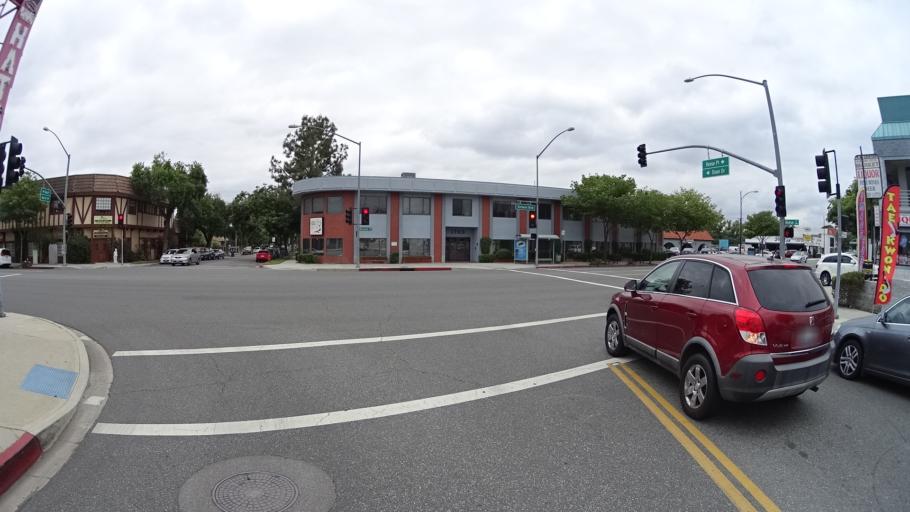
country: US
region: California
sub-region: Los Angeles County
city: Burbank
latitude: 34.1818
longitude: -118.3297
